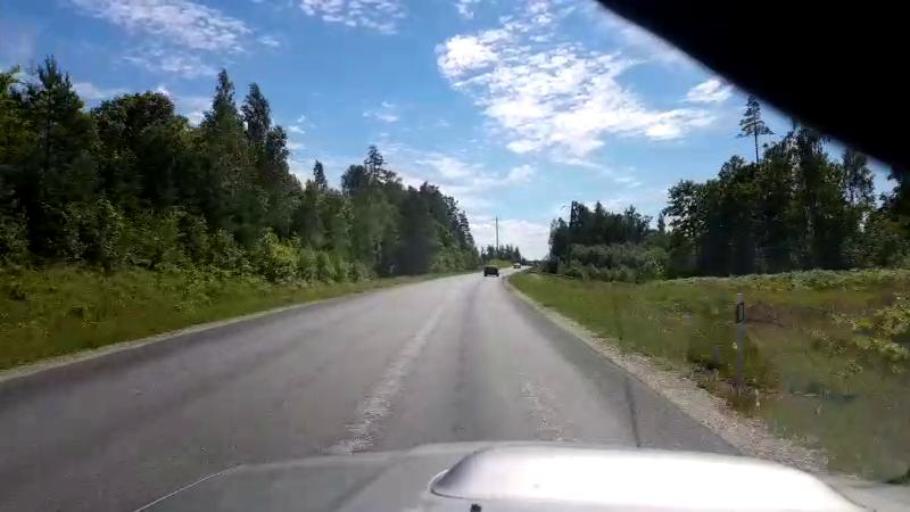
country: EE
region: Jogevamaa
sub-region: Jogeva linn
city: Jogeva
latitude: 58.8406
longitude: 26.2907
